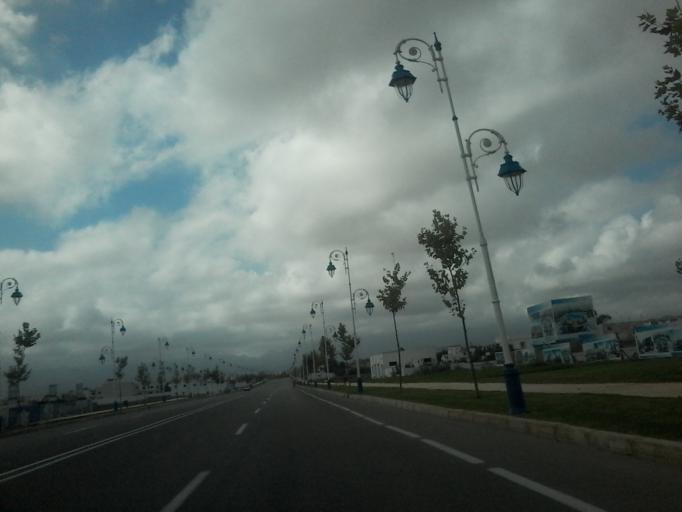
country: MA
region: Tanger-Tetouan
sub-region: Tetouan
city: Martil
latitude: 35.6537
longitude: -5.2944
